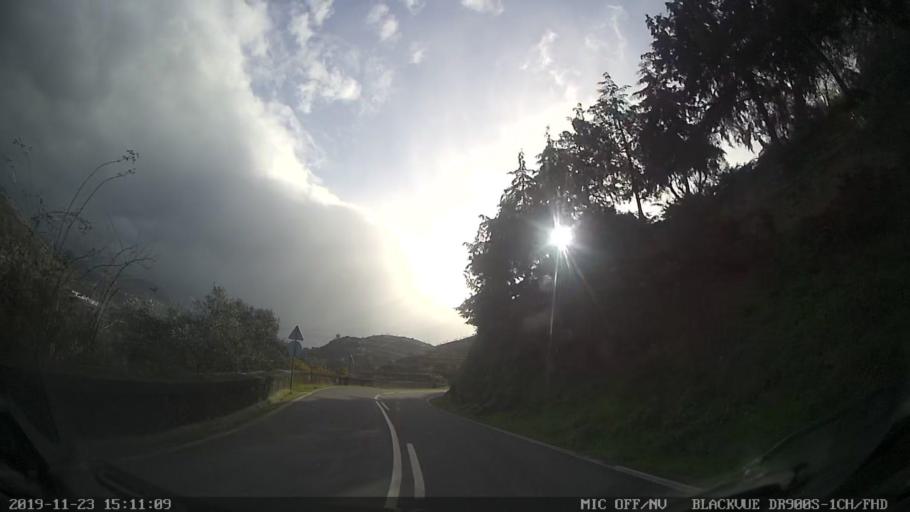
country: PT
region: Vila Real
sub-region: Peso da Regua
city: Peso da Regua
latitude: 41.1397
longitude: -7.7785
